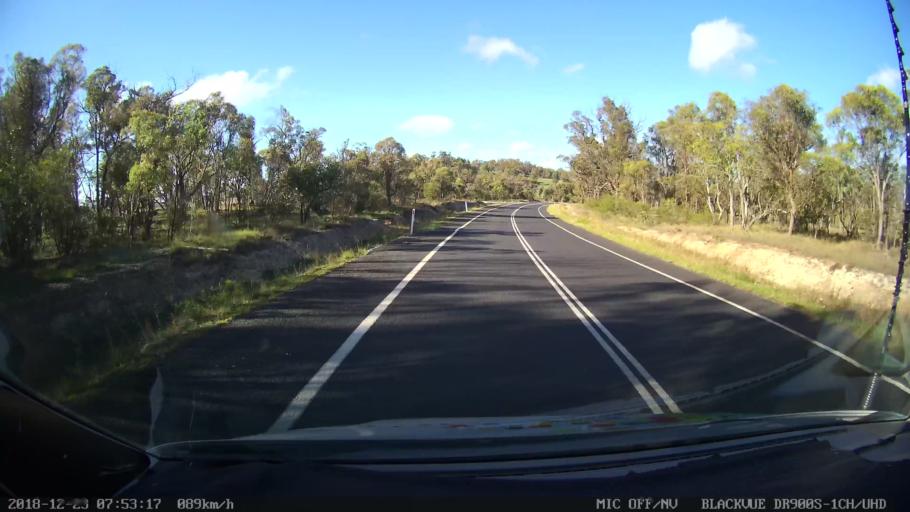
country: AU
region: New South Wales
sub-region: Armidale Dumaresq
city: Armidale
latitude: -30.5358
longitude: 151.8108
